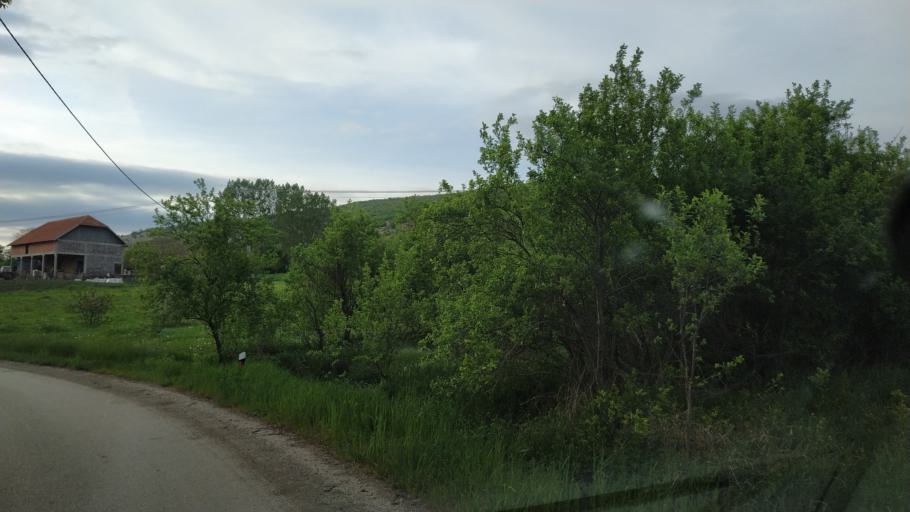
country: RS
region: Central Serbia
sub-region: Zajecarski Okrug
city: Soko Banja
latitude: 43.5252
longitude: 21.8602
